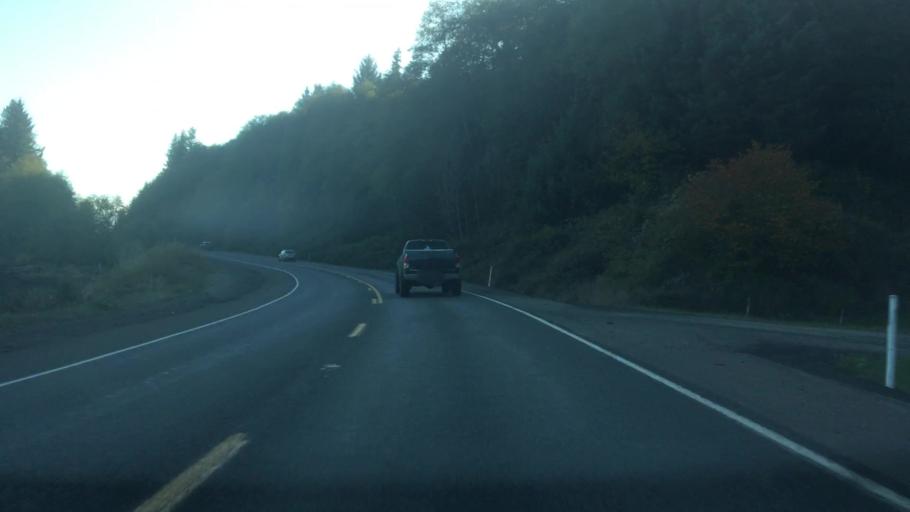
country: US
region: Oregon
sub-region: Clatsop County
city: Astoria
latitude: 46.2592
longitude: -123.8528
